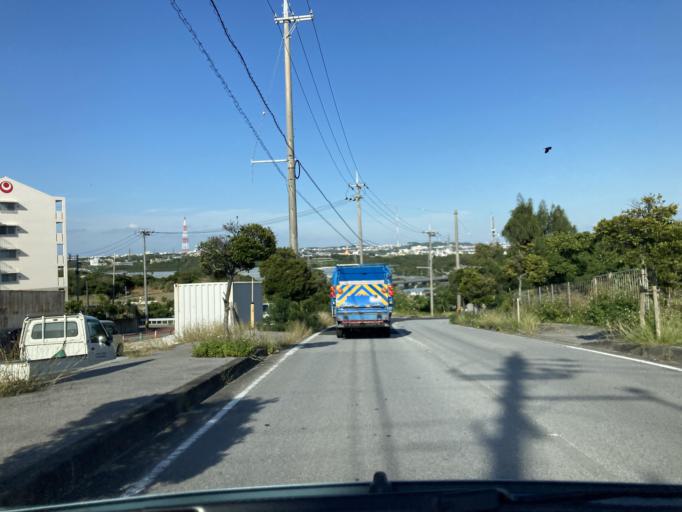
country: JP
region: Okinawa
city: Tomigusuku
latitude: 26.1689
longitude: 127.6982
